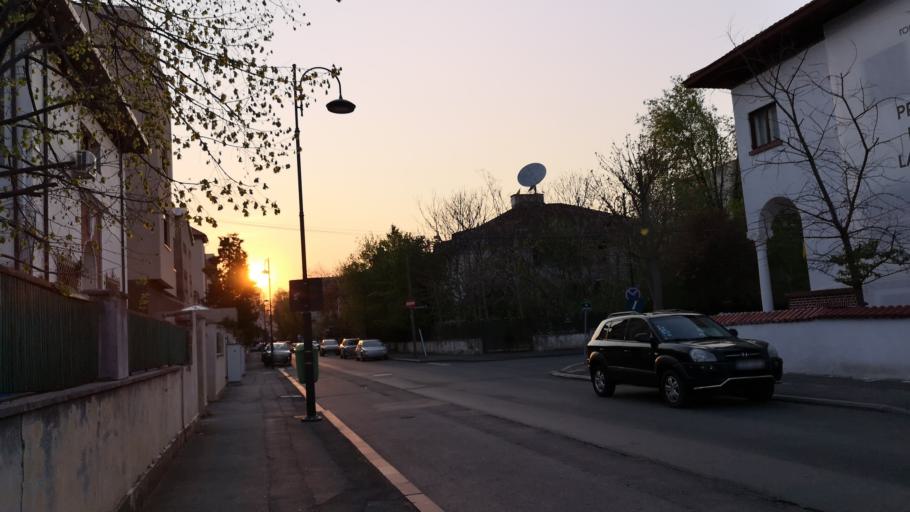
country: RO
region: Bucuresti
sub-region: Municipiul Bucuresti
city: Bucharest
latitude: 44.4607
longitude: 26.0903
